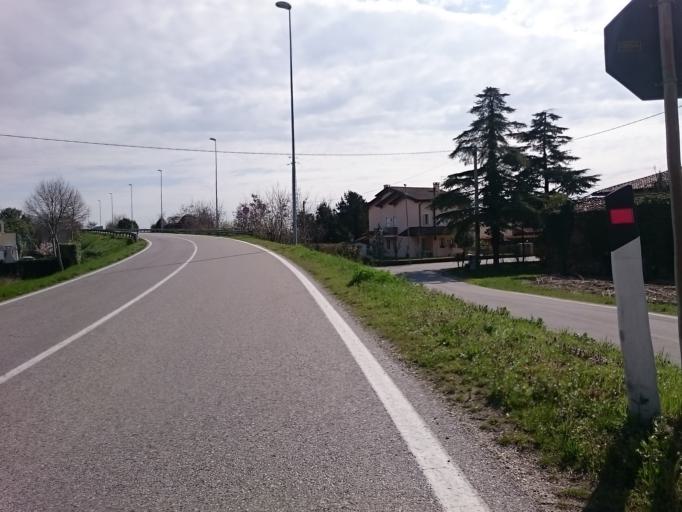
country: IT
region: Veneto
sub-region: Provincia di Padova
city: Mandriola-Sant'Agostino
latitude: 45.3486
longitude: 11.8483
